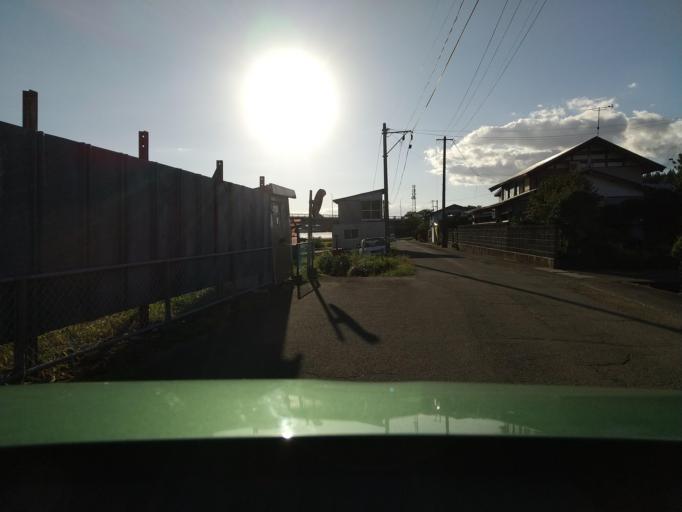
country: JP
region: Akita
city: Kakunodatemachi
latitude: 39.6244
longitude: 140.6310
